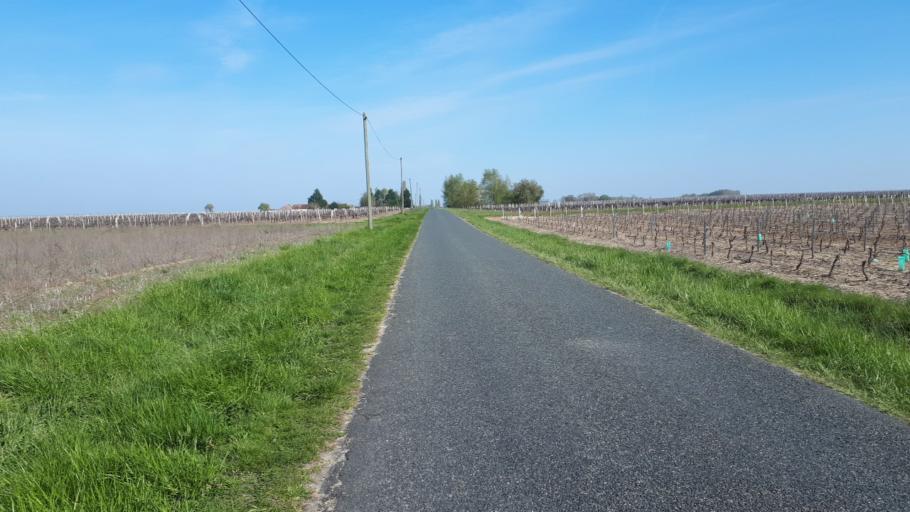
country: FR
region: Centre
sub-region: Departement du Loir-et-Cher
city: Saint-Romain-sur-Cher
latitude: 47.3676
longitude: 1.4011
